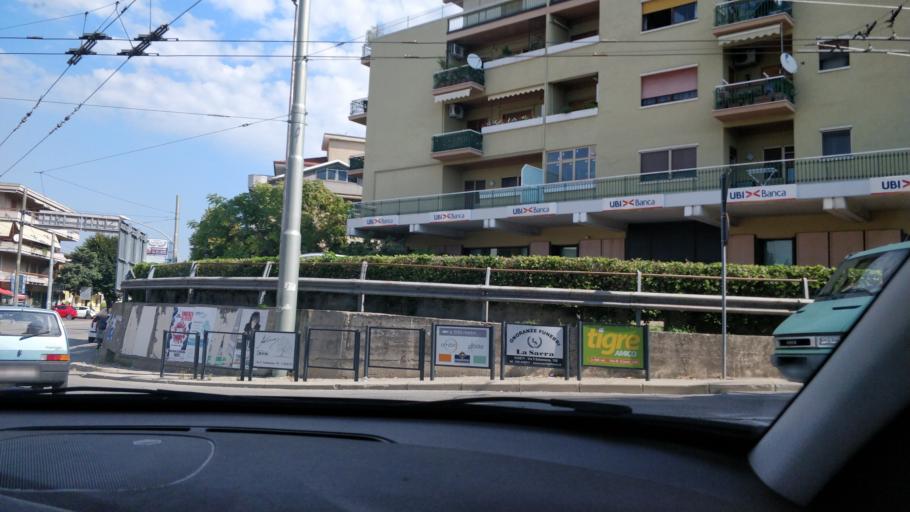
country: IT
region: Abruzzo
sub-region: Provincia di Chieti
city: Chieti
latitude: 42.3726
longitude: 14.1438
